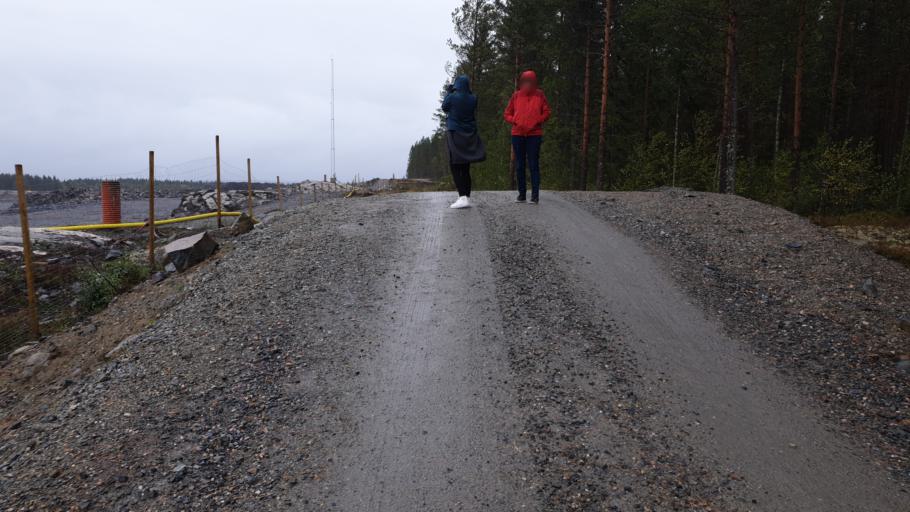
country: SE
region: Vaesterbotten
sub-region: Skelleftea Kommun
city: Soedra Bergsbyn
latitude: 64.7393
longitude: 21.0746
